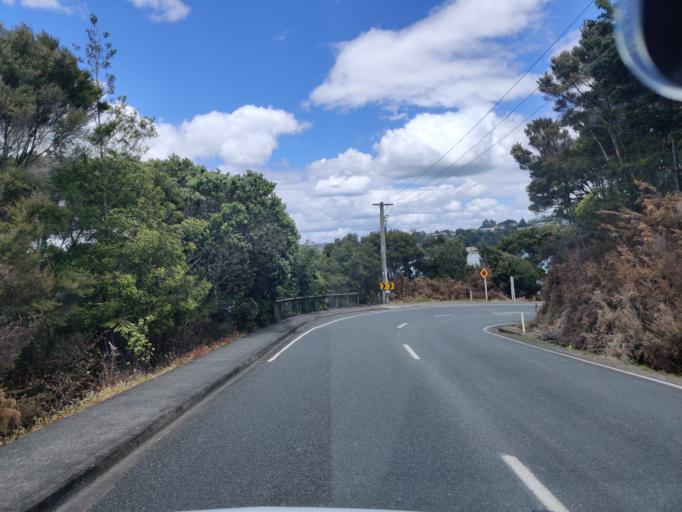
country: NZ
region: Northland
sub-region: Far North District
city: Paihia
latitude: -35.3049
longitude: 174.1207
